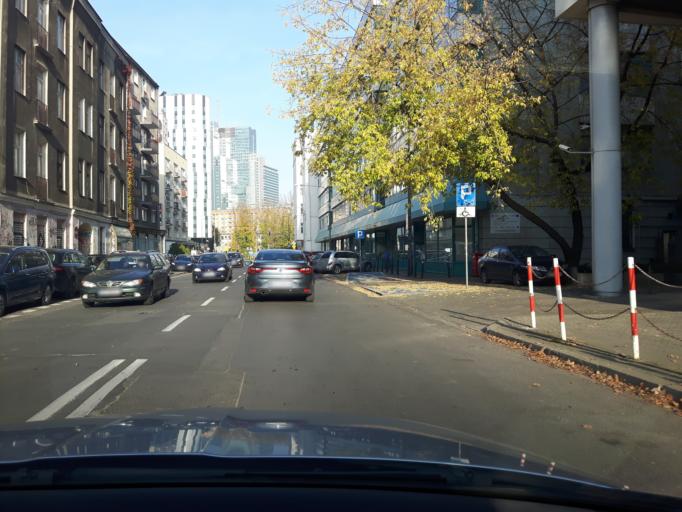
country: PL
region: Masovian Voivodeship
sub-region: Warszawa
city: Ochota
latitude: 52.2280
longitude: 20.9925
